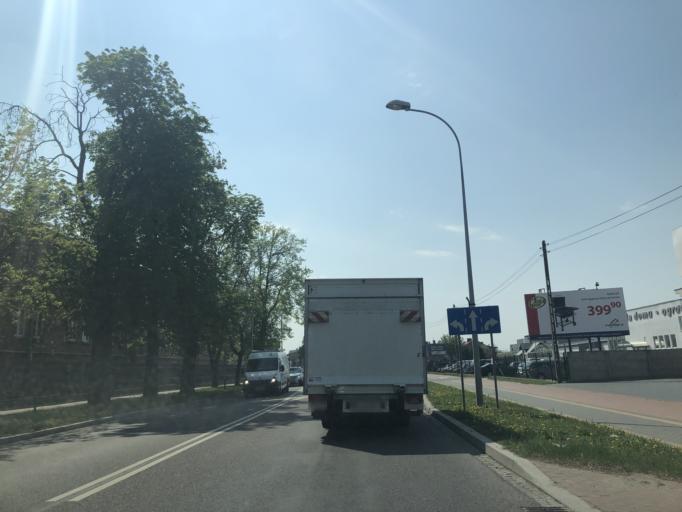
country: PL
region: Podlasie
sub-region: Lomza
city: Lomza
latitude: 53.1629
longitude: 22.0585
